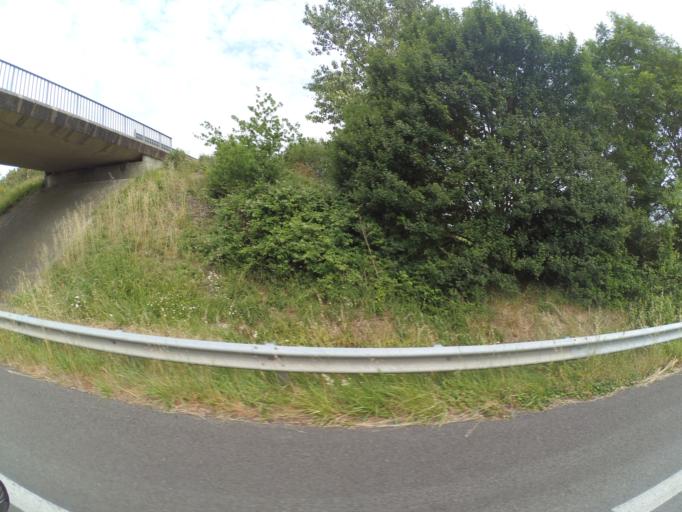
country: FR
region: Pays de la Loire
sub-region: Departement de la Vendee
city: Saint-Georges-de-Montaigu
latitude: 46.9349
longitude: -1.3144
